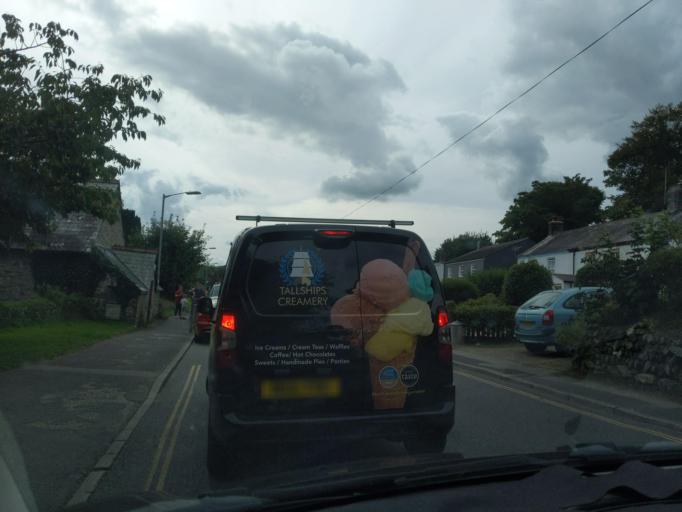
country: GB
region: England
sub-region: Cornwall
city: St Austell
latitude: 50.3369
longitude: -4.7602
